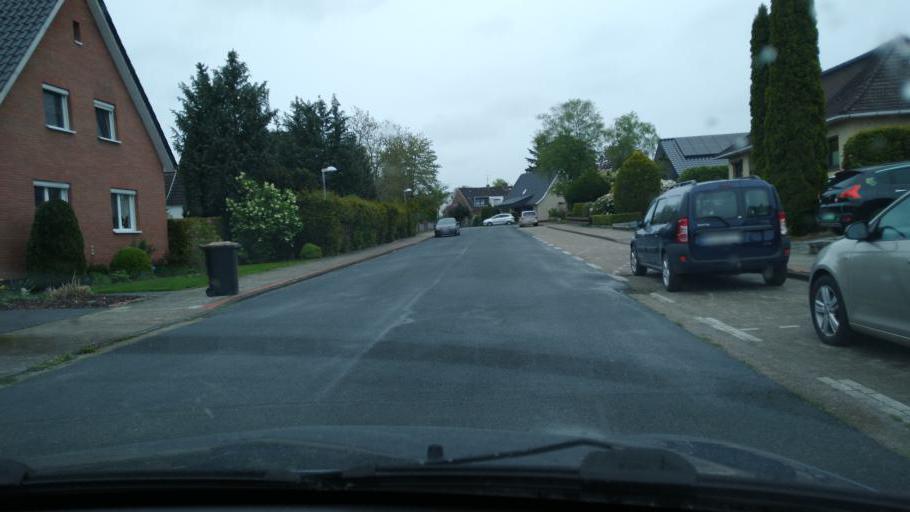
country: DE
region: Lower Saxony
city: Loxstedt
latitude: 53.4835
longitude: 8.6941
